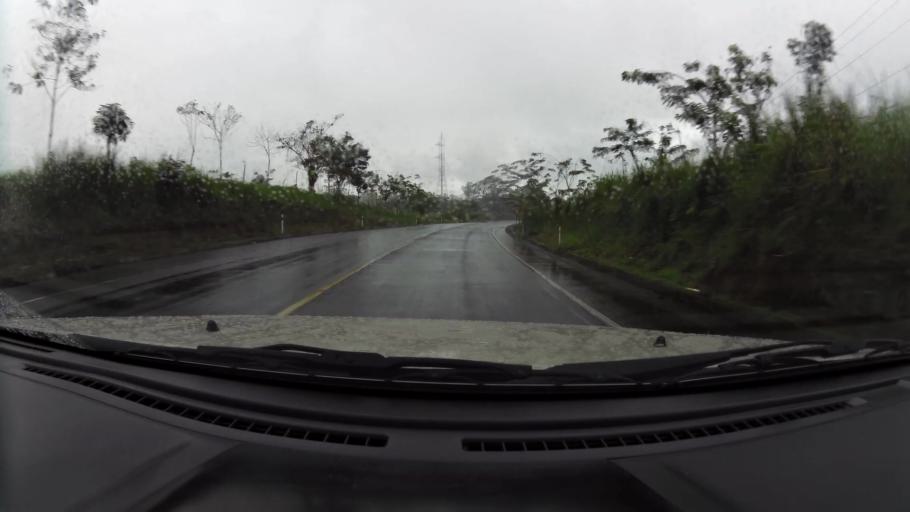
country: EC
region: Santo Domingo de los Tsachilas
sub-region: Canton Santo Domingo de los Colorados
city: Santo Domingo de los Colorados
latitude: -0.2314
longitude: -79.1243
